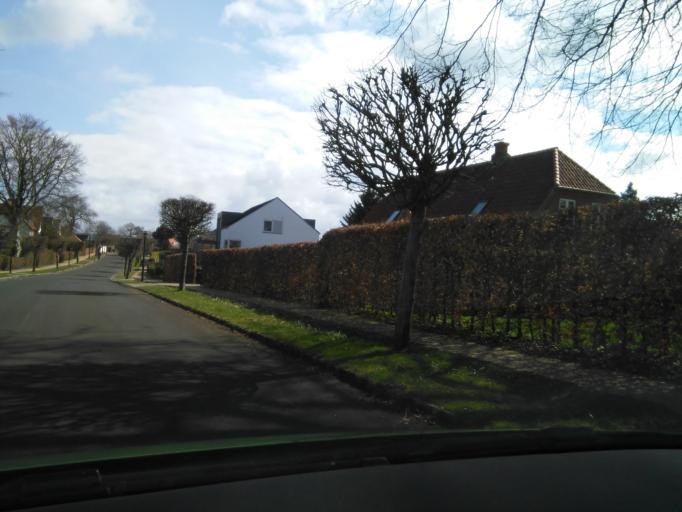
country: DK
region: South Denmark
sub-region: Middelfart Kommune
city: Strib
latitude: 55.5430
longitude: 9.7646
